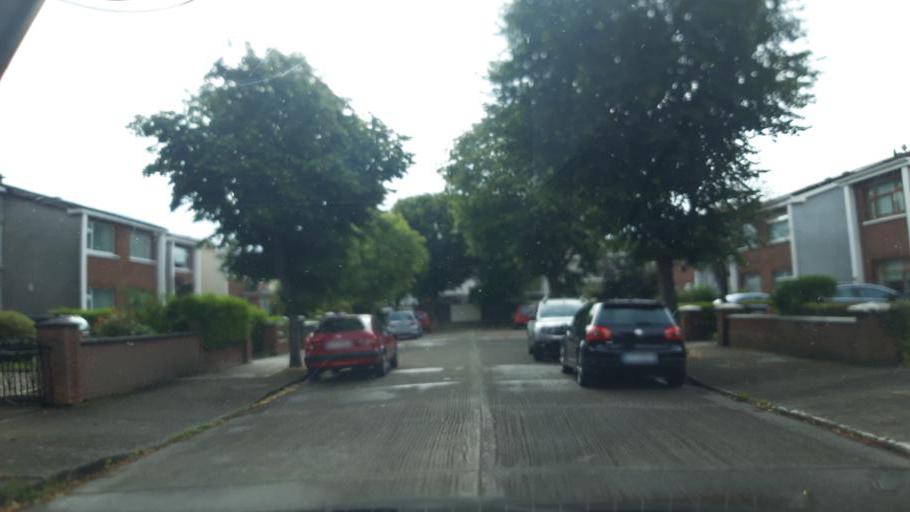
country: IE
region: Leinster
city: Marino
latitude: 53.3767
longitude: -6.2290
